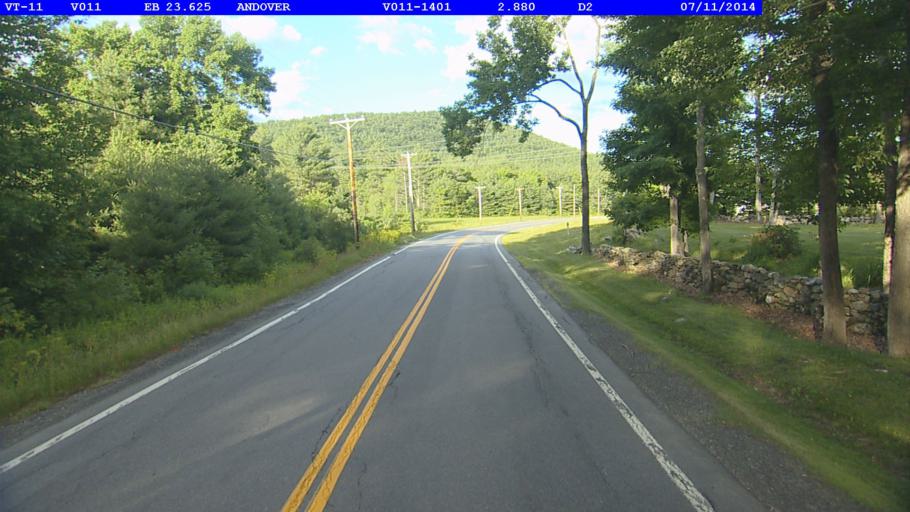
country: US
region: Vermont
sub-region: Windsor County
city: Chester
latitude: 43.2624
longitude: -72.6978
